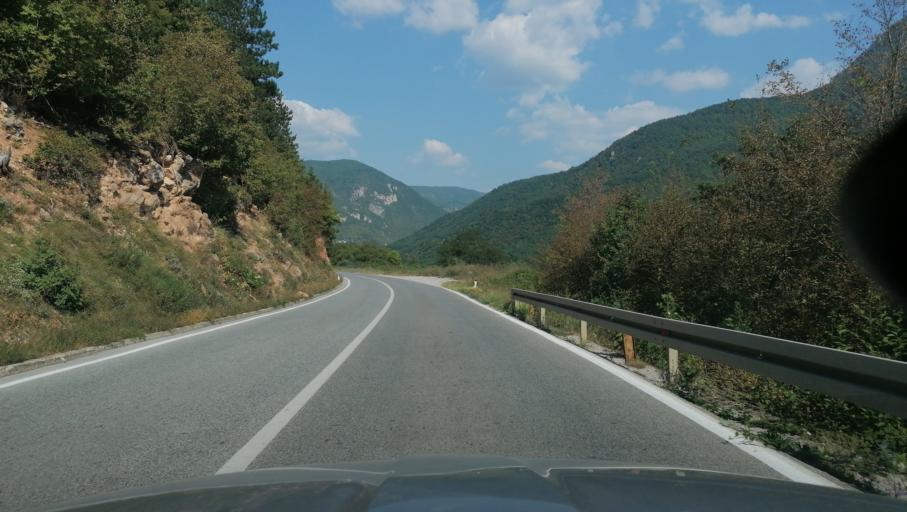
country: BA
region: Federation of Bosnia and Herzegovina
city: Gorazde
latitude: 43.6778
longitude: 19.0631
